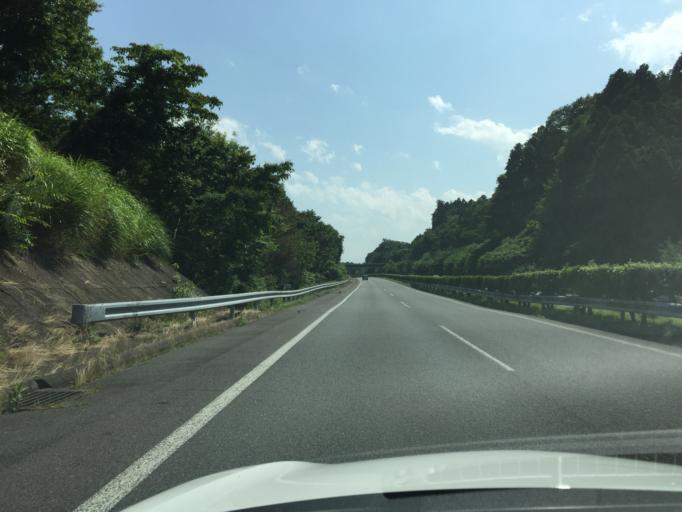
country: JP
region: Fukushima
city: Iwaki
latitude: 36.9506
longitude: 140.7765
